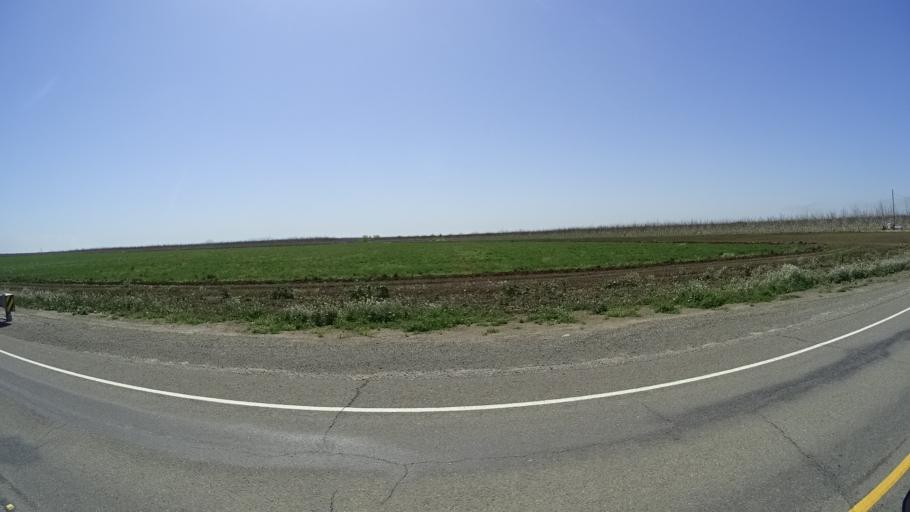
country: US
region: California
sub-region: Butte County
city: Durham
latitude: 39.4643
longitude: -121.9555
